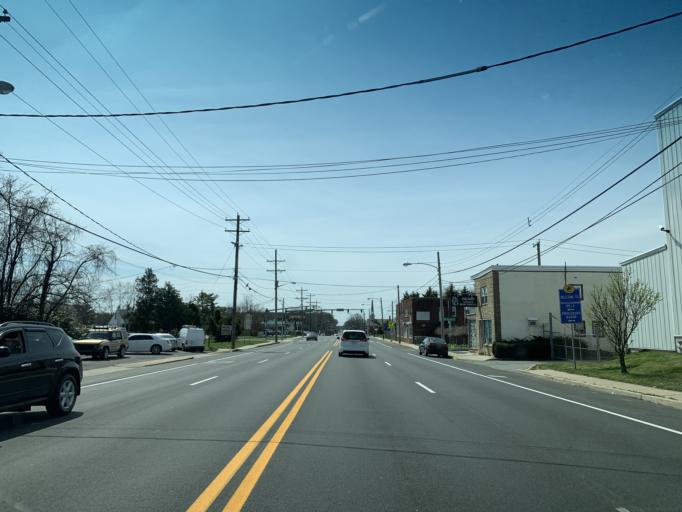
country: US
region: Delaware
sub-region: New Castle County
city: Elsmere
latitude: 39.7253
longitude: -75.5905
